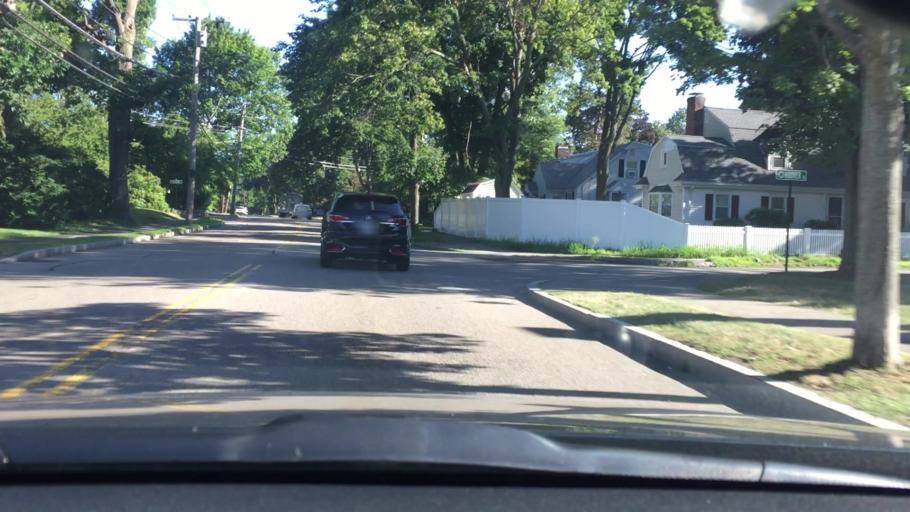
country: US
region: Massachusetts
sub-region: Norfolk County
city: Needham
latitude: 42.2905
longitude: -71.2314
